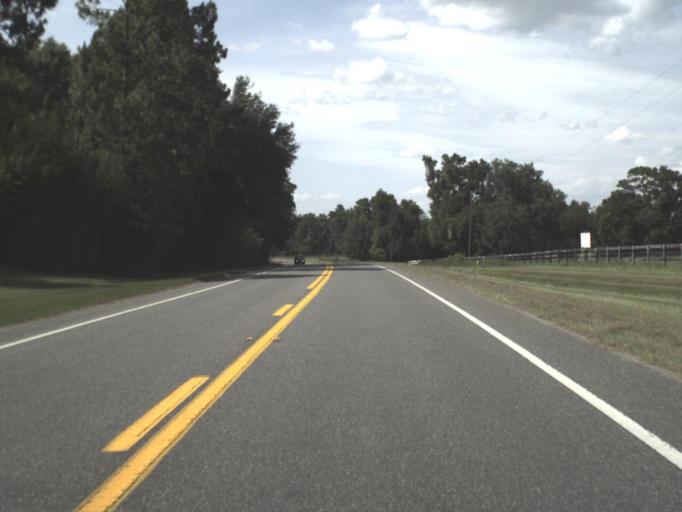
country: US
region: Florida
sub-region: Alachua County
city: High Springs
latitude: 29.9706
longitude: -82.7101
